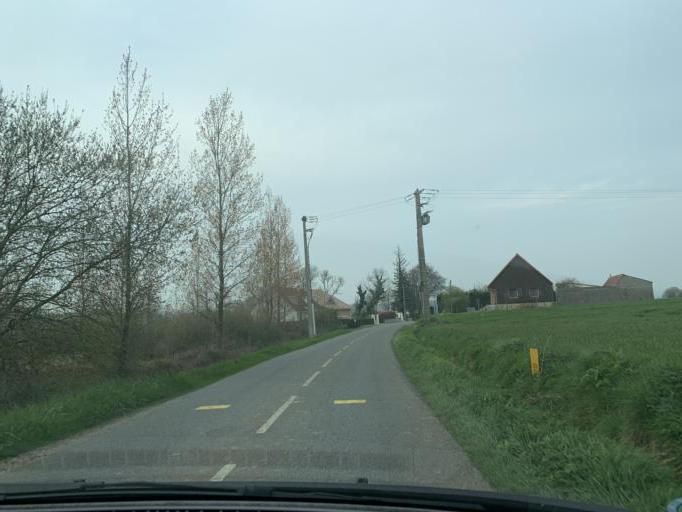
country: FR
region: Nord-Pas-de-Calais
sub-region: Departement du Pas-de-Calais
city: Samer
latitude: 50.6562
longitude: 1.7518
